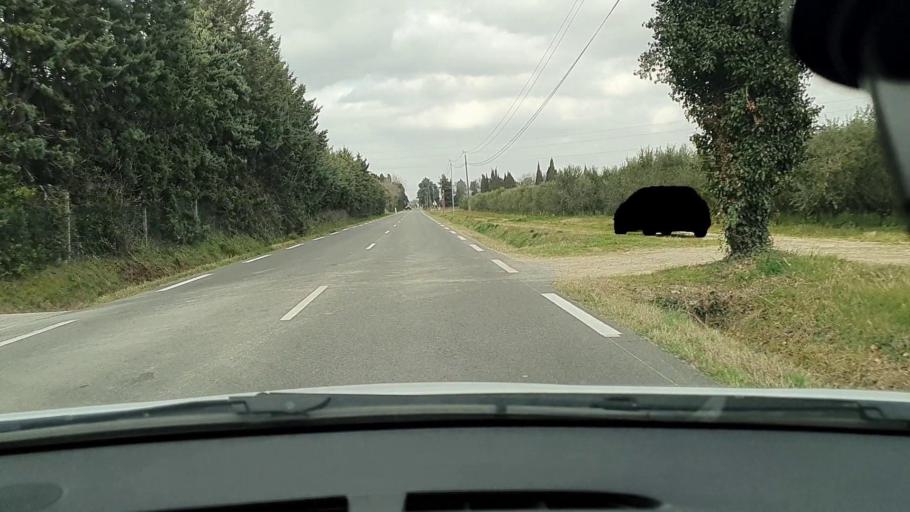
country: FR
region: Languedoc-Roussillon
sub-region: Departement du Gard
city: Meynes
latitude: 43.8910
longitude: 4.5743
